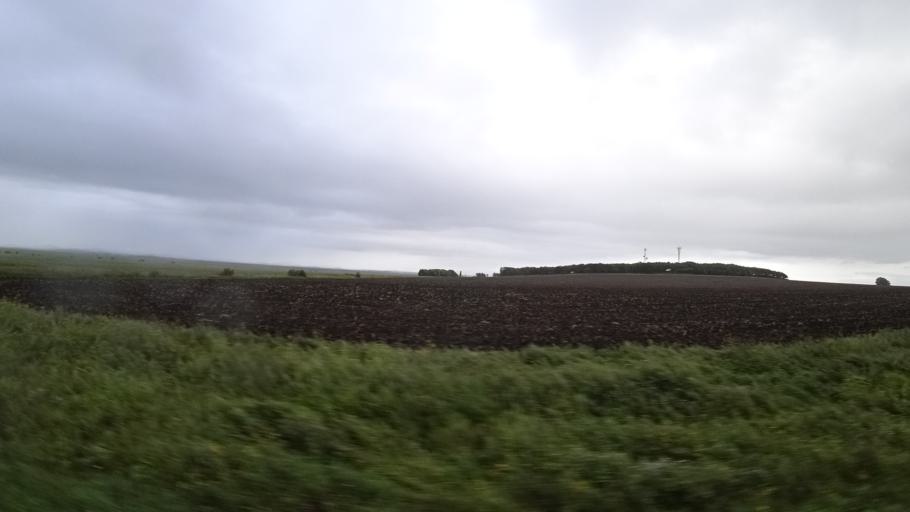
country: RU
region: Primorskiy
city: Chernigovka
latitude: 44.3719
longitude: 132.5299
